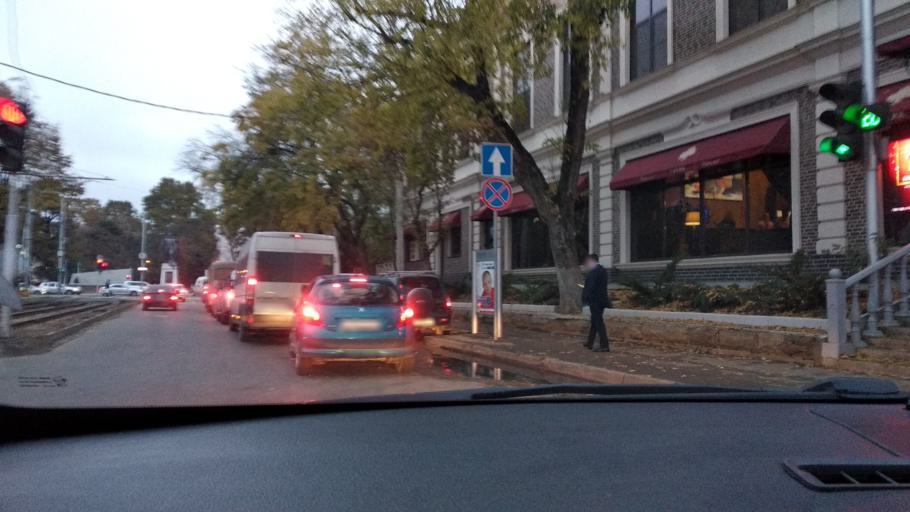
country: RU
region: Krasnodarskiy
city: Krasnodar
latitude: 45.0134
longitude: 38.9699
